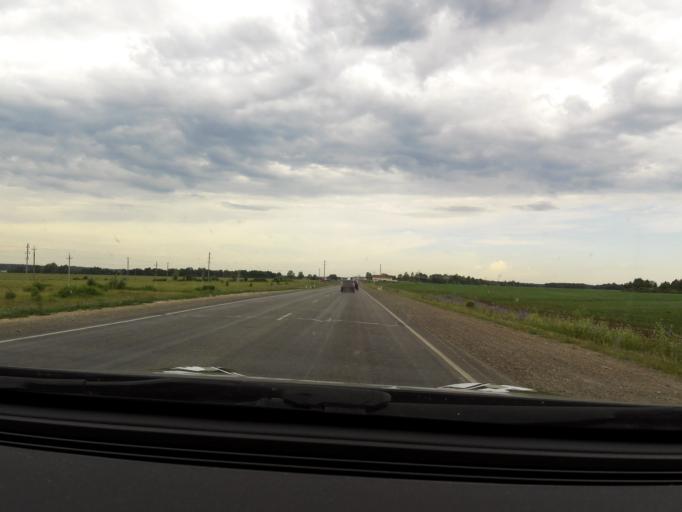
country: RU
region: Bashkortostan
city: Kudeyevskiy
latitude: 54.8169
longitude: 56.7465
